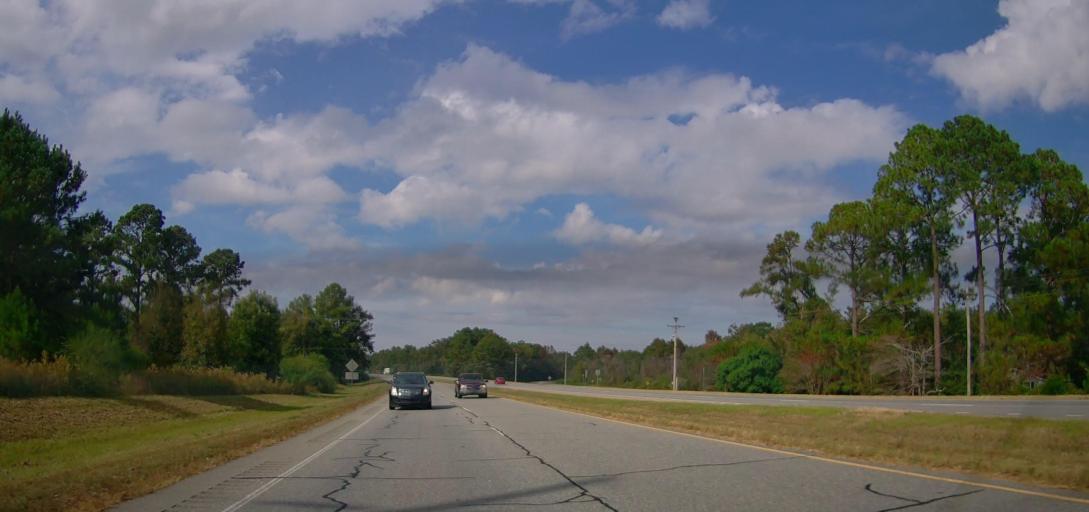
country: US
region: Georgia
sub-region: Mitchell County
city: Pelham
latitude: 31.1726
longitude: -84.1473
